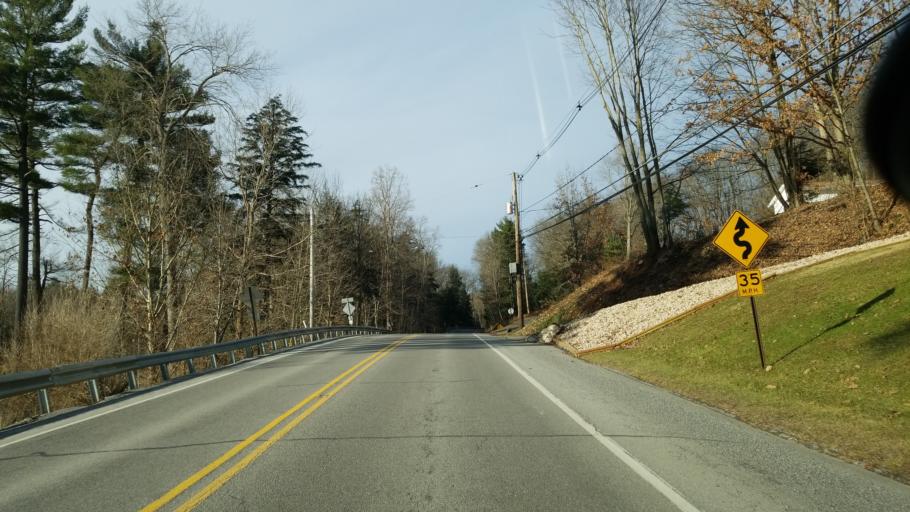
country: US
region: Pennsylvania
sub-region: Clearfield County
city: Curwensville
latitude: 40.9680
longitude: -78.6173
